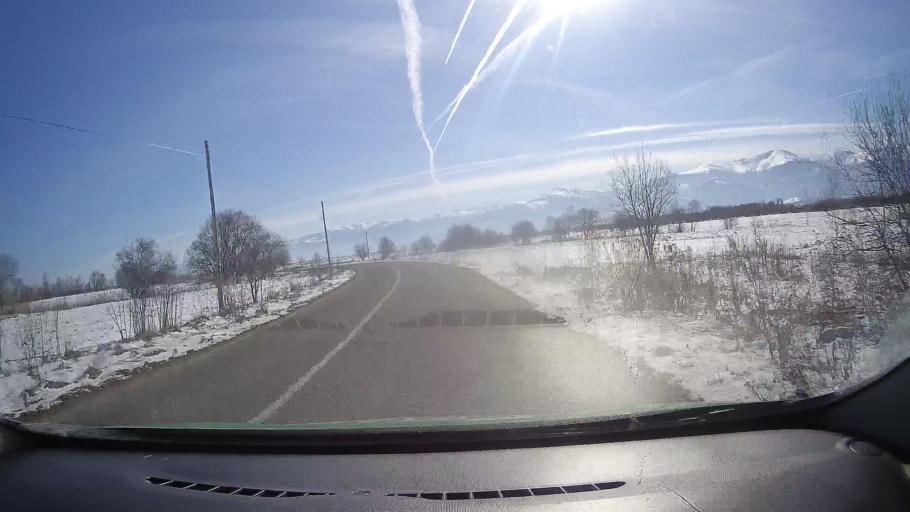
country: RO
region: Brasov
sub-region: Comuna Sambata de Sus
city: Sambata de Sus
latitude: 45.7479
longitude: 24.8392
